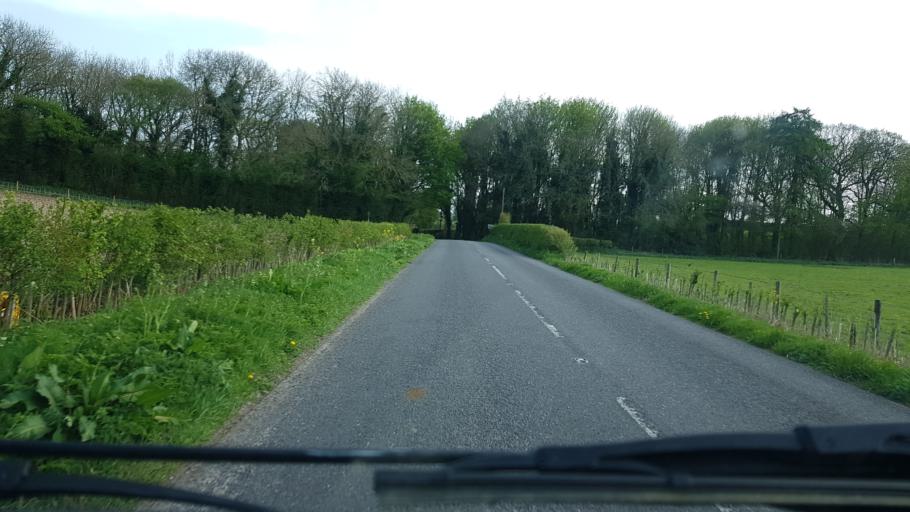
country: GB
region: England
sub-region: Hampshire
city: Kingsclere
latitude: 51.2926
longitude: -1.2662
